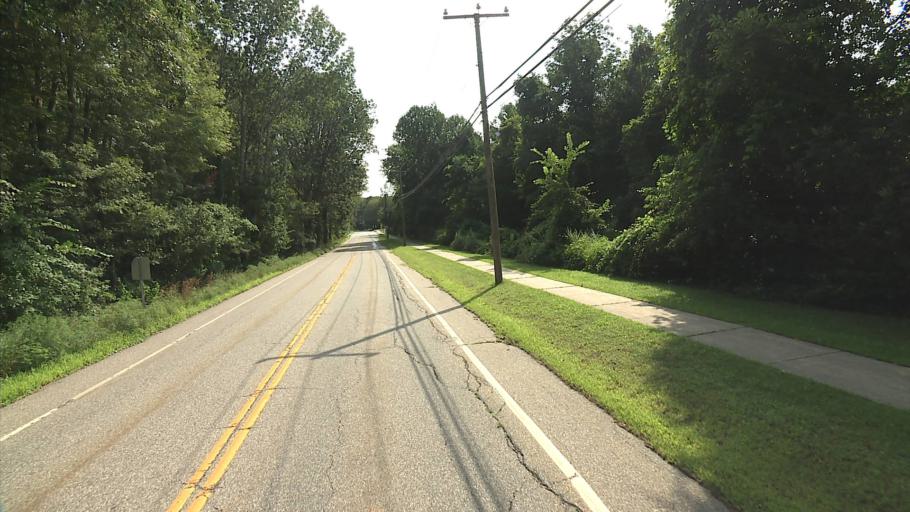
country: US
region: Connecticut
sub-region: New London County
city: Colchester
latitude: 41.5740
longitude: -72.3053
